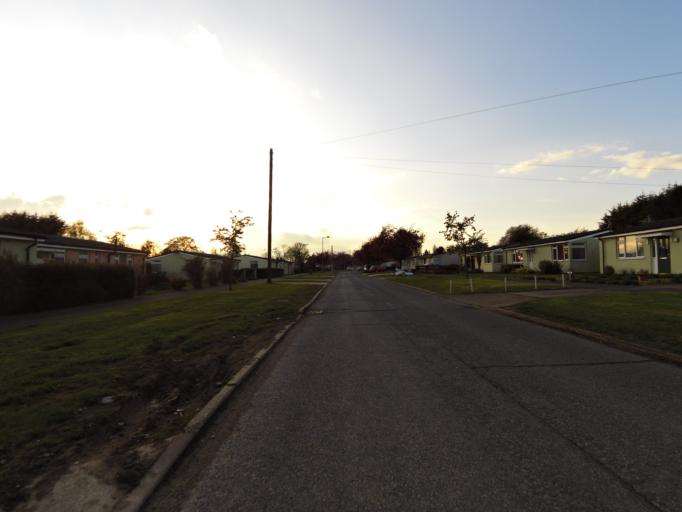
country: GB
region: England
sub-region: Suffolk
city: Ipswich
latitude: 52.0741
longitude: 1.1864
